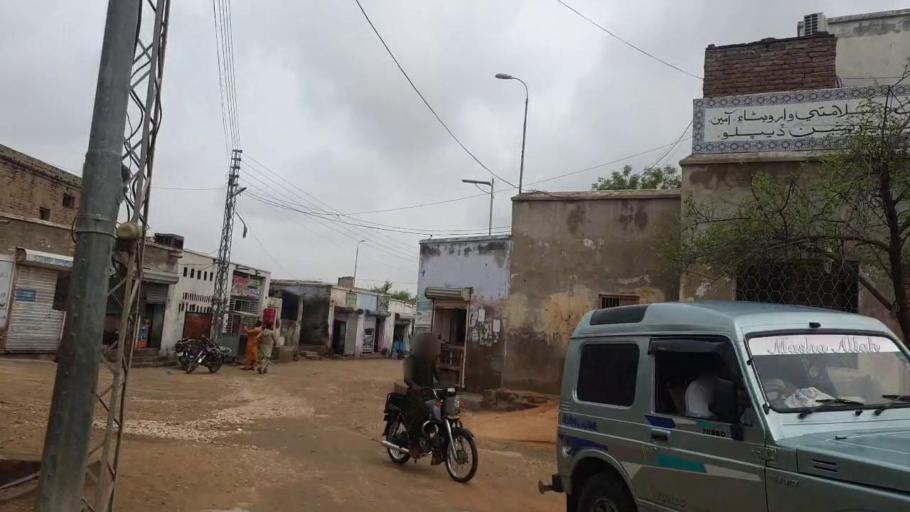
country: PK
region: Sindh
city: Diplo
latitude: 24.4683
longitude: 69.5808
